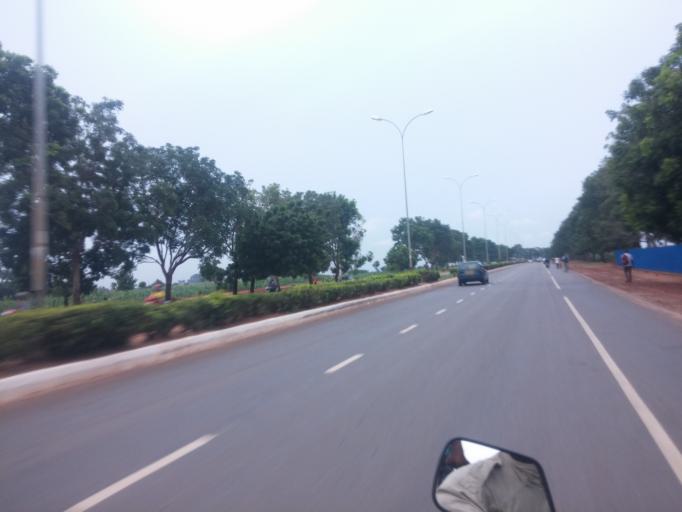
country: TG
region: Maritime
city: Lome
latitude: 6.1948
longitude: 1.2144
